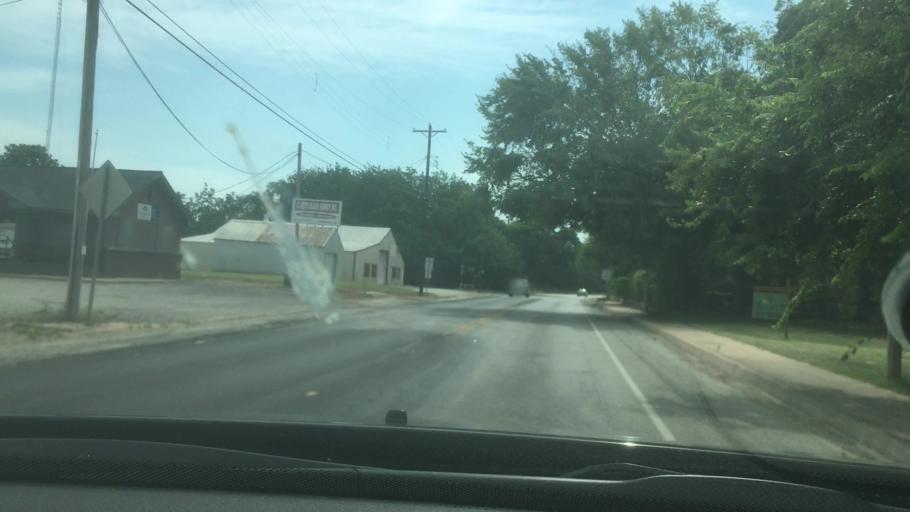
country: US
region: Oklahoma
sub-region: Garvin County
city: Maysville
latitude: 34.8172
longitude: -97.4038
